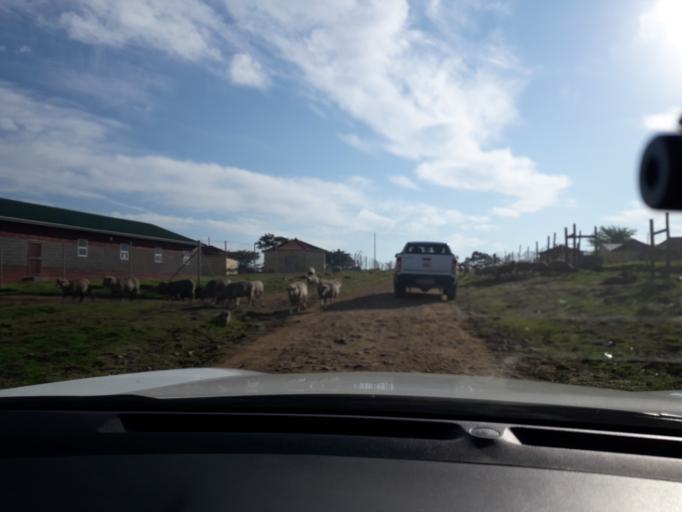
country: ZA
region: Eastern Cape
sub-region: Buffalo City Metropolitan Municipality
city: Bhisho
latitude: -32.9382
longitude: 27.2902
